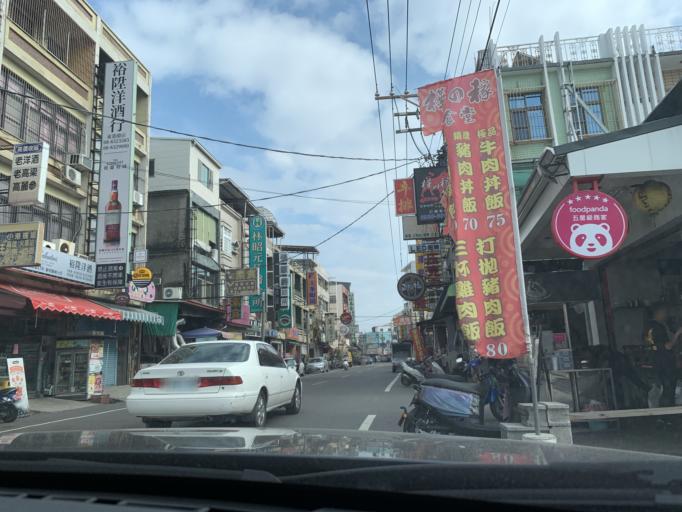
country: TW
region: Taiwan
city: Fengshan
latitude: 22.4681
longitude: 120.4514
